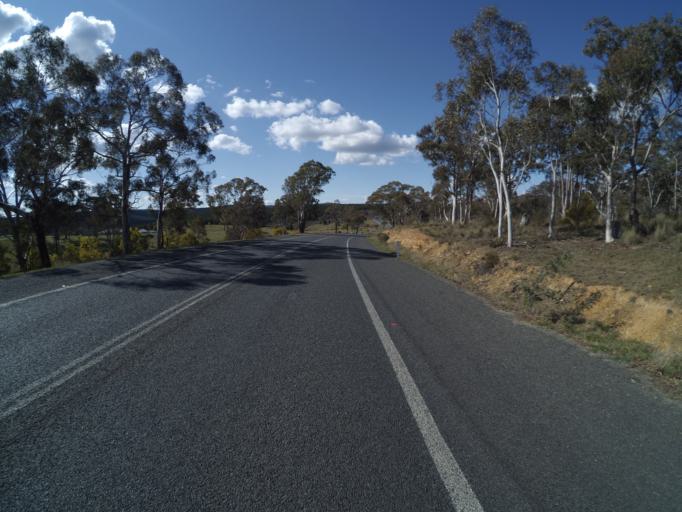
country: AU
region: New South Wales
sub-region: Queanbeyan
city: Queanbeyan
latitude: -35.3416
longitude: 149.2836
